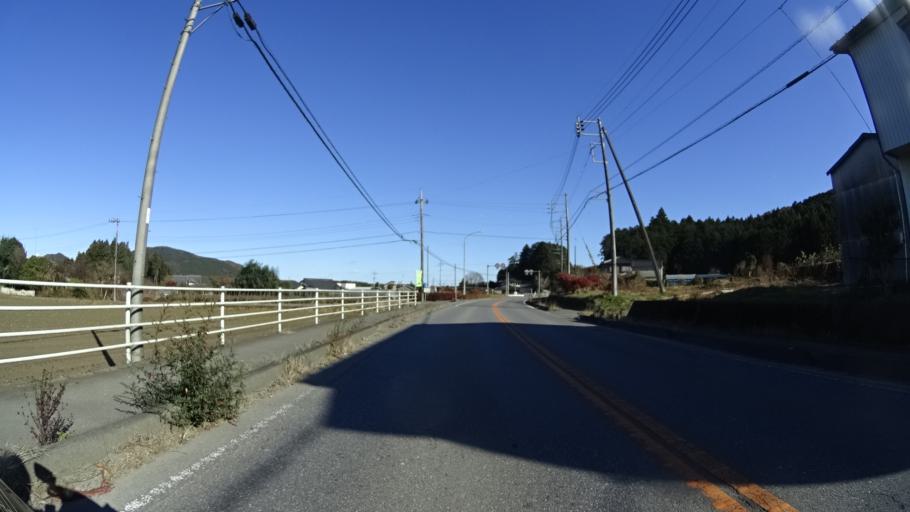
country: JP
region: Tochigi
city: Kanuma
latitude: 36.5868
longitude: 139.7816
